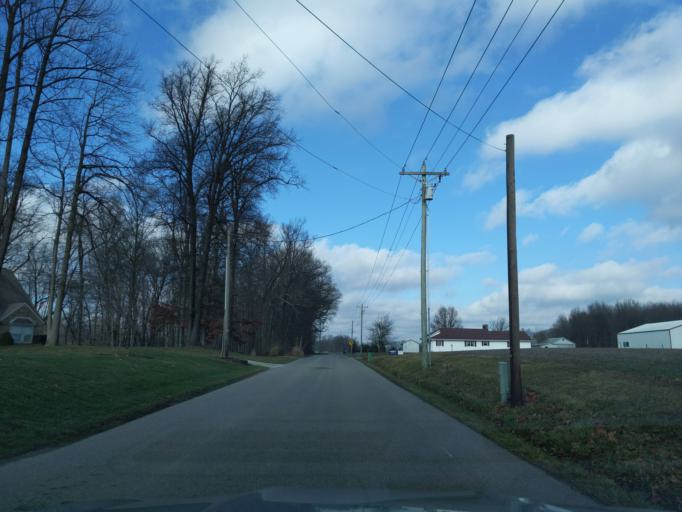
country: US
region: Indiana
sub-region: Ripley County
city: Batesville
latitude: 39.3280
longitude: -85.3257
